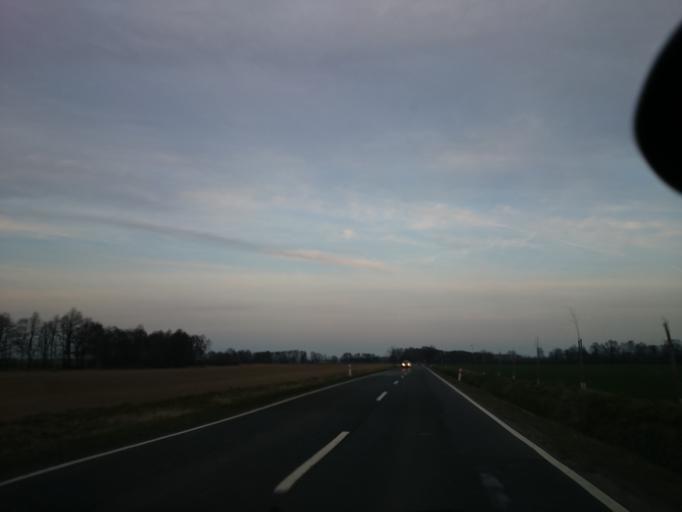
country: PL
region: Opole Voivodeship
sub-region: Powiat prudnicki
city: Moszczanka
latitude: 50.3222
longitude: 17.4458
